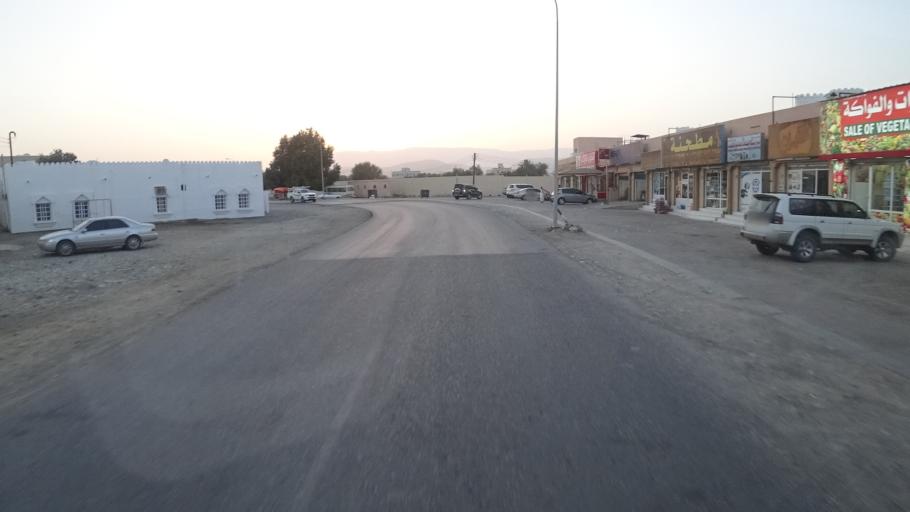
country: OM
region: Ash Sharqiyah
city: Sur
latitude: 22.5399
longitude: 59.4897
